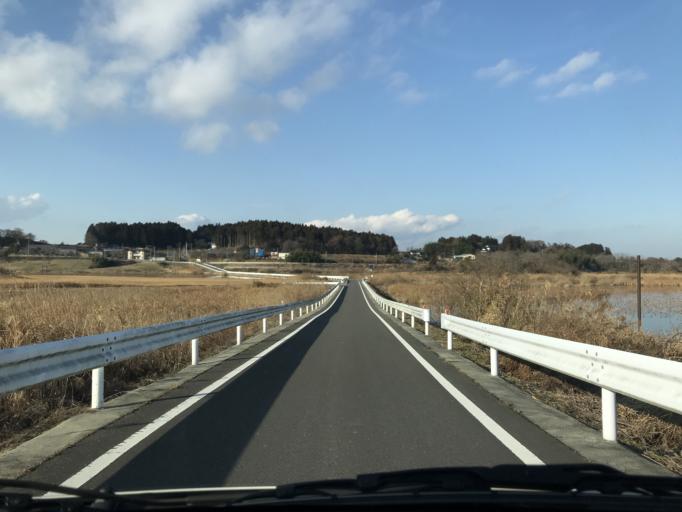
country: JP
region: Miyagi
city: Wakuya
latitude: 38.6801
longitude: 141.1166
